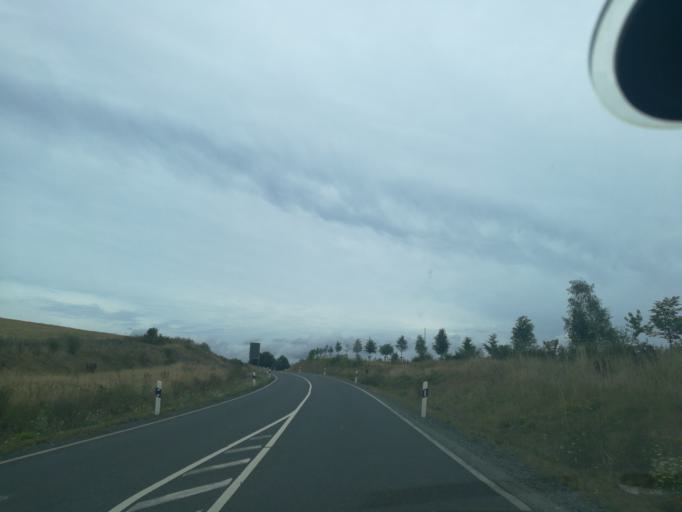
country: DE
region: Bavaria
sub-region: Upper Franconia
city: Regnitzlosau
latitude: 50.3350
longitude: 12.0832
